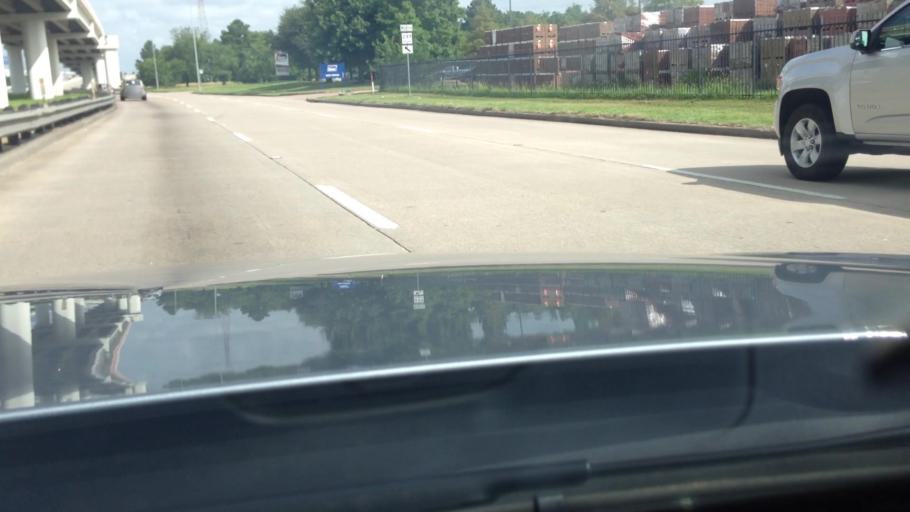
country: US
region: Texas
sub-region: Harris County
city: Hudson
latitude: 29.9395
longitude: -95.5189
